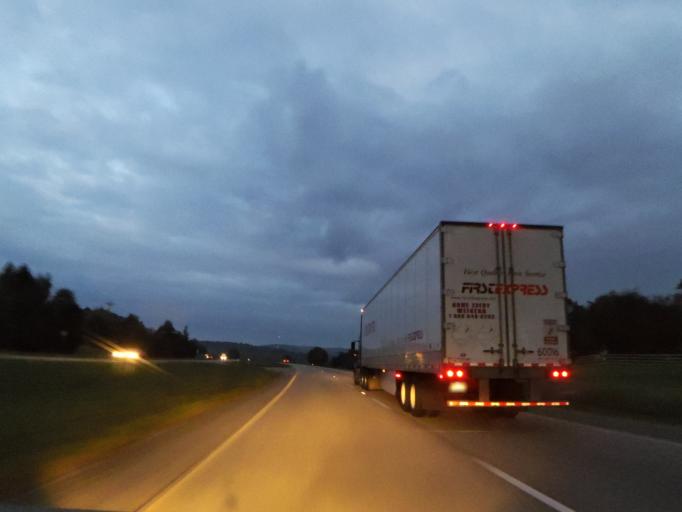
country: US
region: Alabama
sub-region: Madison County
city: New Hope
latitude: 34.6061
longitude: -86.2585
